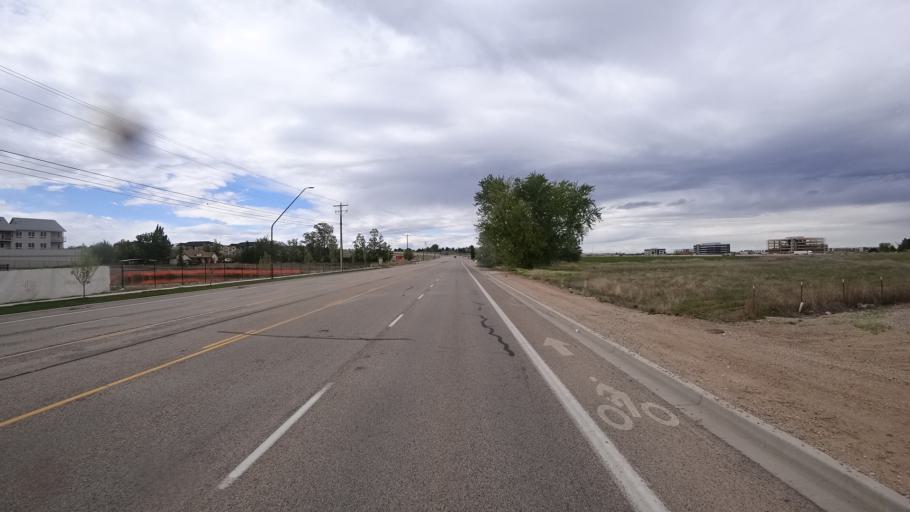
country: US
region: Idaho
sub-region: Ada County
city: Meridian
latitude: 43.5902
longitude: -116.4190
